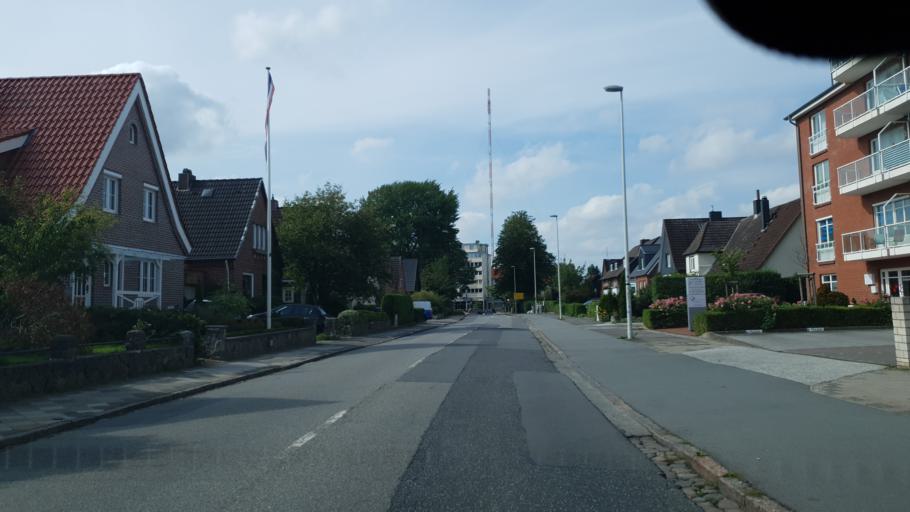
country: DE
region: Schleswig-Holstein
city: Kronshagen
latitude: 54.3321
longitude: 10.0774
